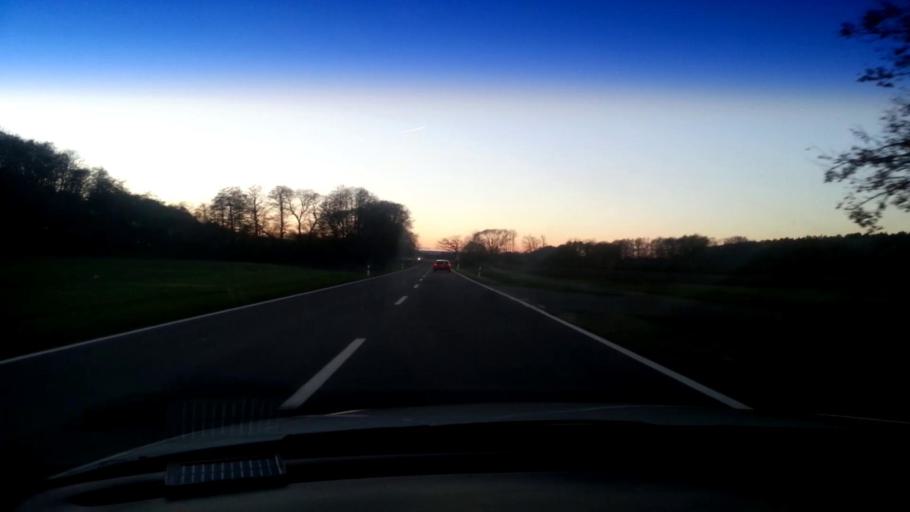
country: DE
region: Bavaria
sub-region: Upper Franconia
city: Memmelsdorf
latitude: 49.9172
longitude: 10.9777
